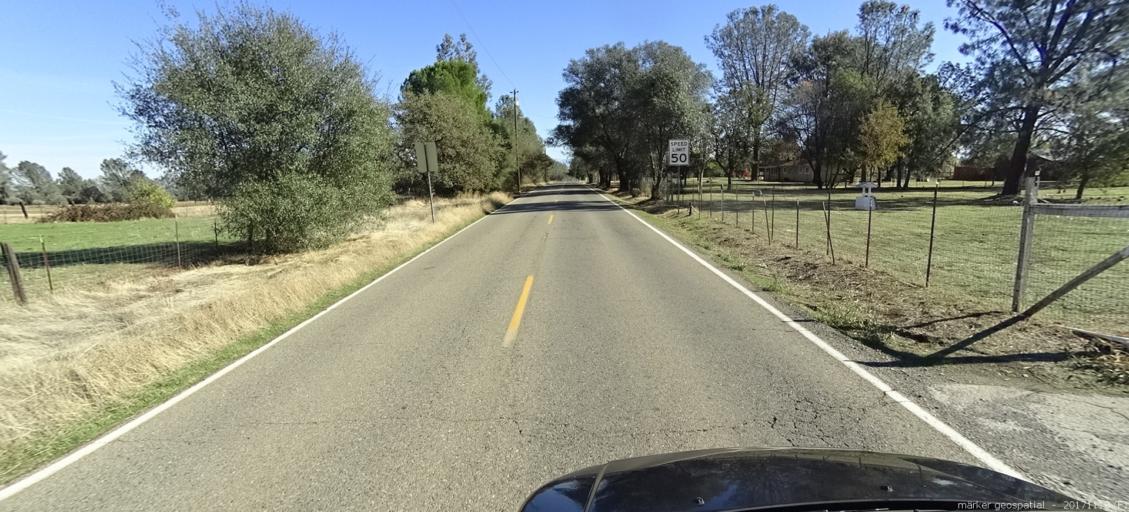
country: US
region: California
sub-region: Shasta County
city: Anderson
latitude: 40.4390
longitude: -122.3907
